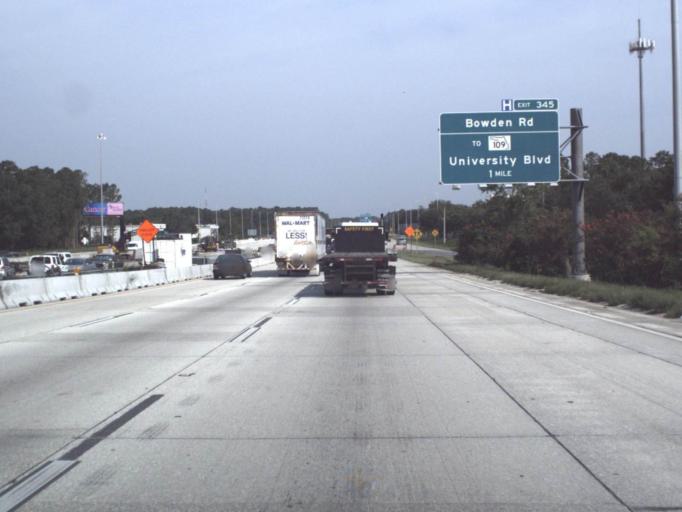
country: US
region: Florida
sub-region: Duval County
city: Jacksonville
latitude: 30.2500
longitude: -81.5948
